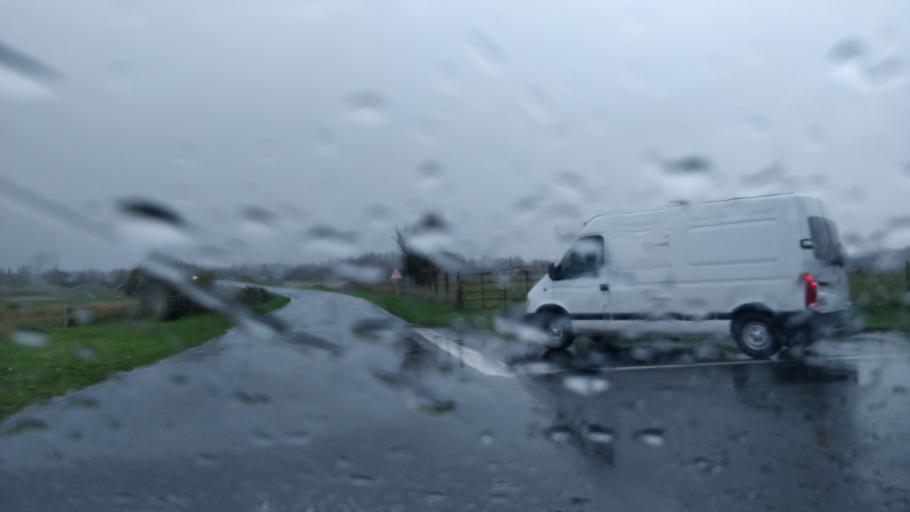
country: FR
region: Lower Normandy
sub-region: Departement de la Manche
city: Brehal
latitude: 48.9016
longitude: -1.5572
